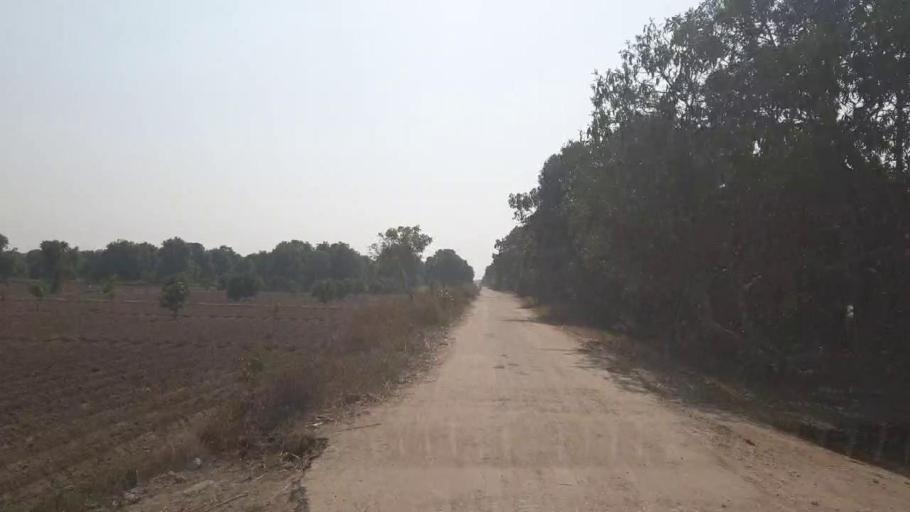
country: PK
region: Sindh
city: Tando Allahyar
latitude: 25.4873
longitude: 68.8351
